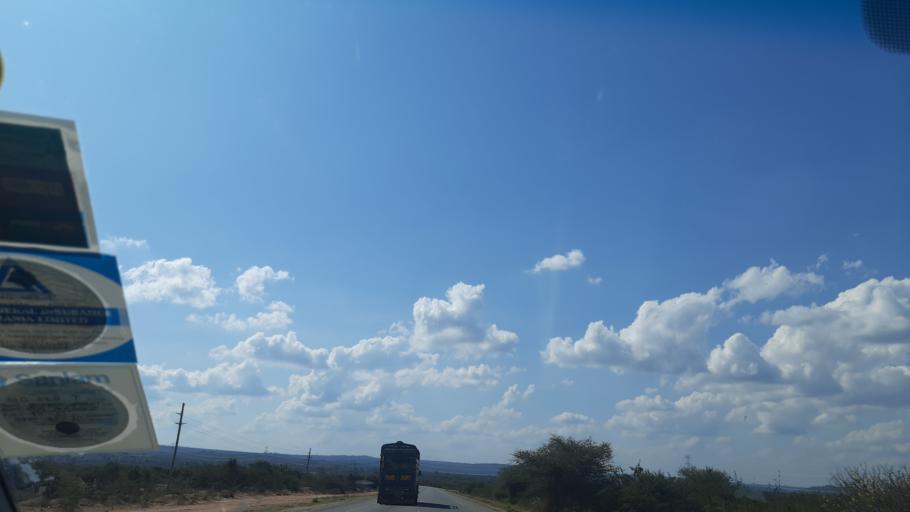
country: TZ
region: Singida
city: Kilimatinde
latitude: -5.7913
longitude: 34.9187
